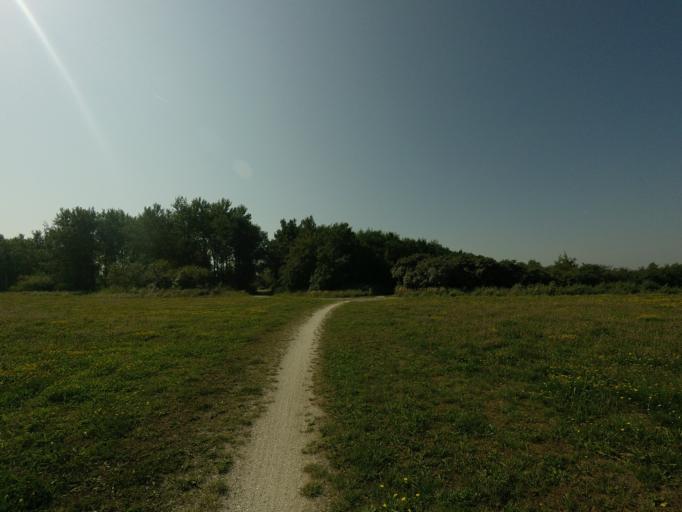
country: NL
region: Groningen
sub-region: Gemeente De Marne
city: Ulrum
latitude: 53.3945
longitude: 6.2541
